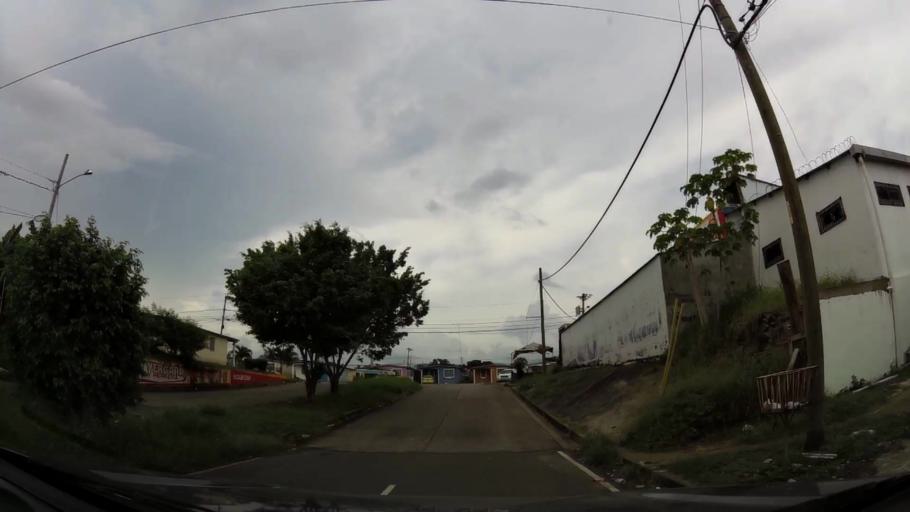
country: PA
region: Panama
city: Cabra Numero Uno
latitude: 9.0908
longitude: -79.3536
